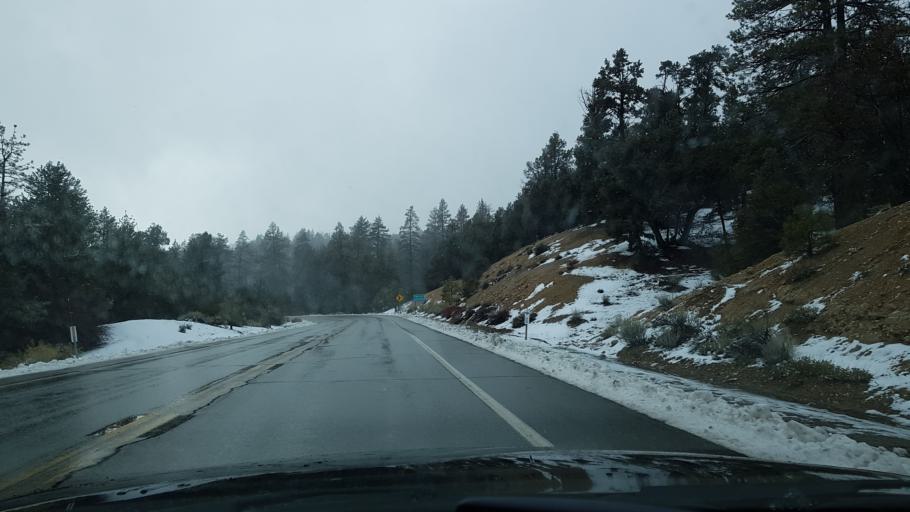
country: US
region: California
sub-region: San Bernardino County
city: Big Bear Lake
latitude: 34.2647
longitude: -116.9180
